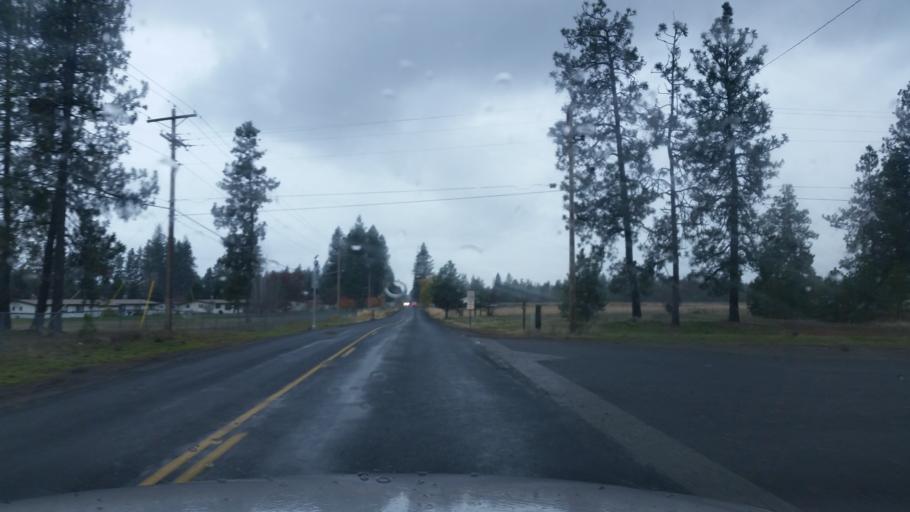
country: US
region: Washington
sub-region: Spokane County
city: Spokane
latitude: 47.5945
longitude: -117.4914
